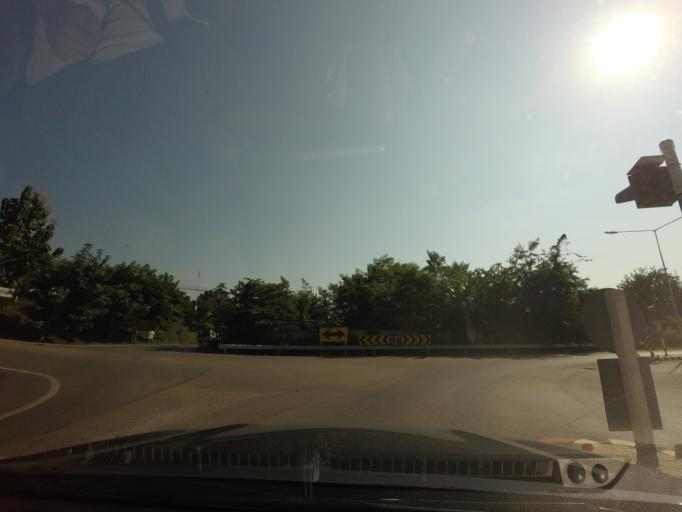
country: TH
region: Nan
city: Nan
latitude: 18.7915
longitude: 100.7949
